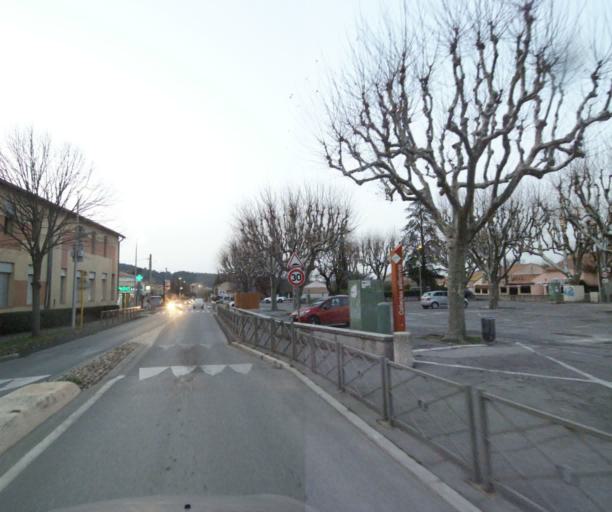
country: FR
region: Provence-Alpes-Cote d'Azur
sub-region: Departement des Bouches-du-Rhone
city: Gardanne
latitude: 43.4347
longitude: 5.4649
